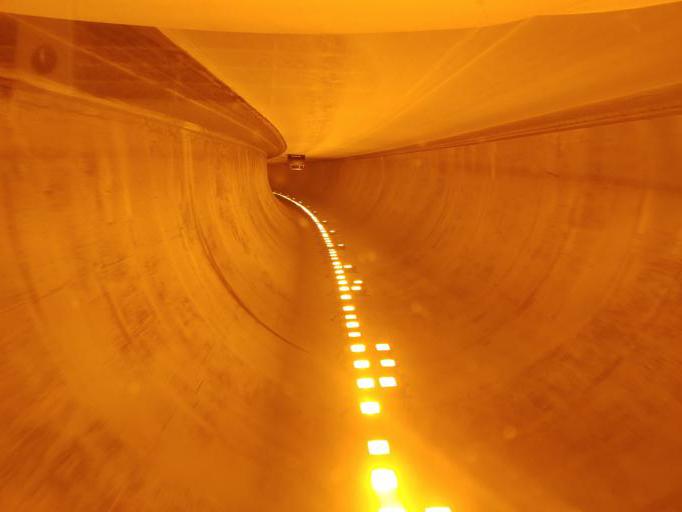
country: US
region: Oregon
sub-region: Lane County
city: Oakridge
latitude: 43.6143
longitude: -122.1335
